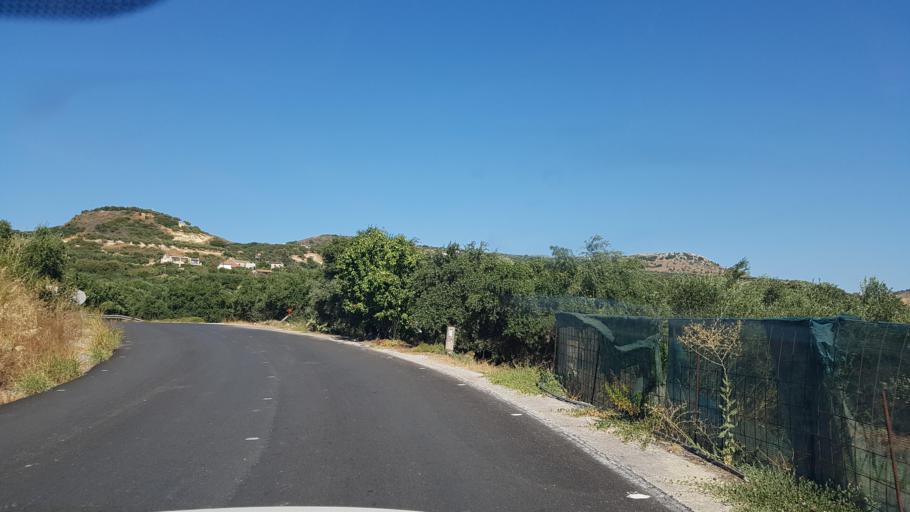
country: GR
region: Crete
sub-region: Nomos Chanias
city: Kissamos
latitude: 35.4950
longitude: 23.7205
